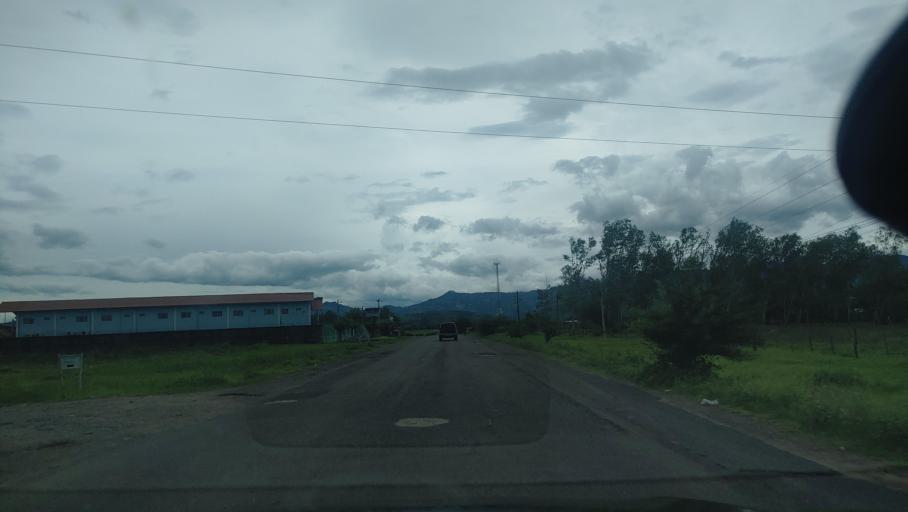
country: HN
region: Choluteca
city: Santa Ana de Yusguare
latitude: 13.3388
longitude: -87.1281
